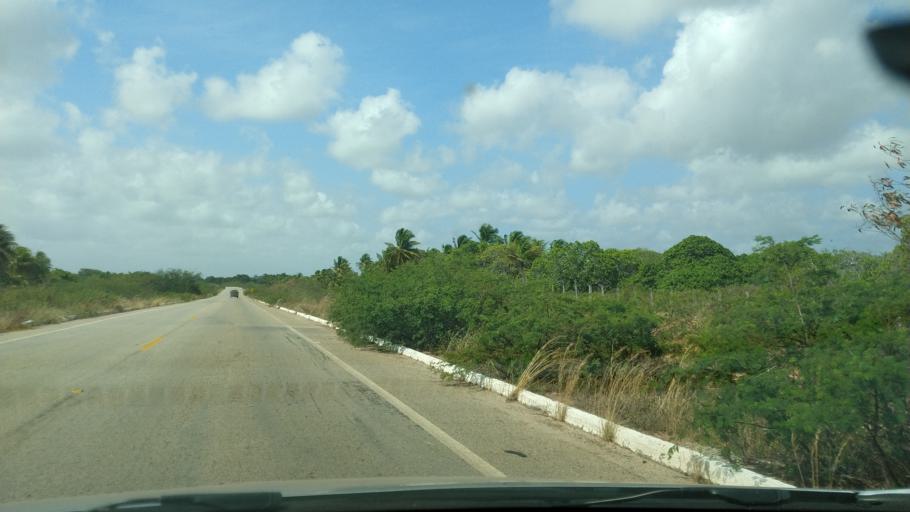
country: BR
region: Rio Grande do Norte
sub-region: Touros
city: Touros
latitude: -5.1776
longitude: -35.5096
